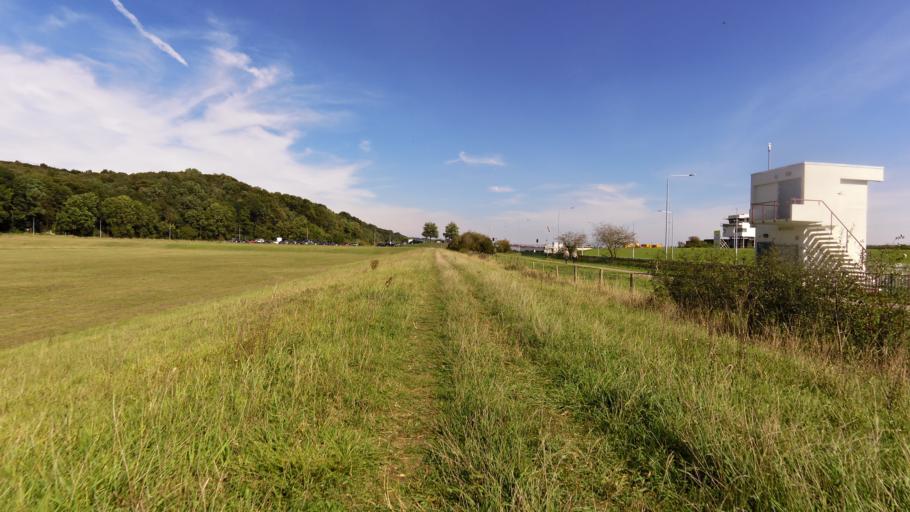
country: NL
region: Gelderland
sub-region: Gemeente Overbetuwe
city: Driel
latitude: 51.9671
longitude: 5.8043
